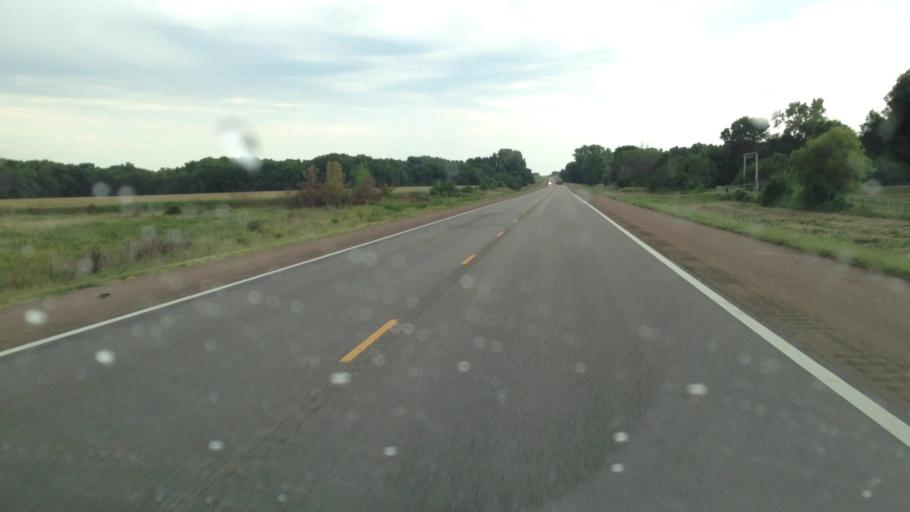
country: US
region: Kansas
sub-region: Woodson County
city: Yates Center
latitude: 38.0333
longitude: -95.7390
